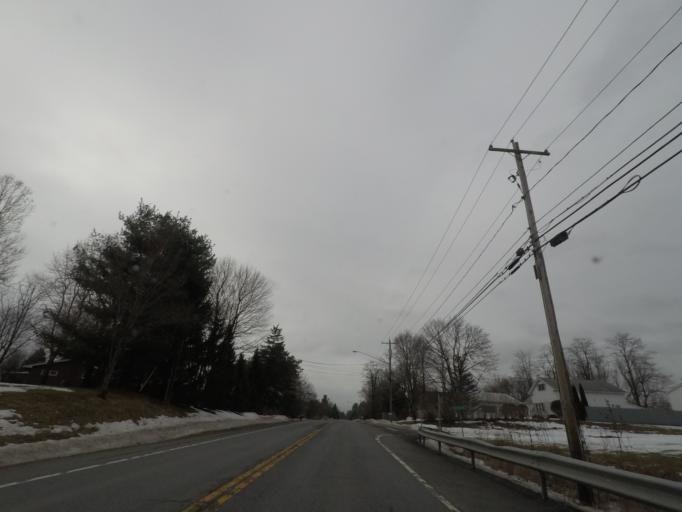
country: US
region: New York
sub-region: Schenectady County
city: Rotterdam
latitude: 42.7216
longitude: -73.9489
